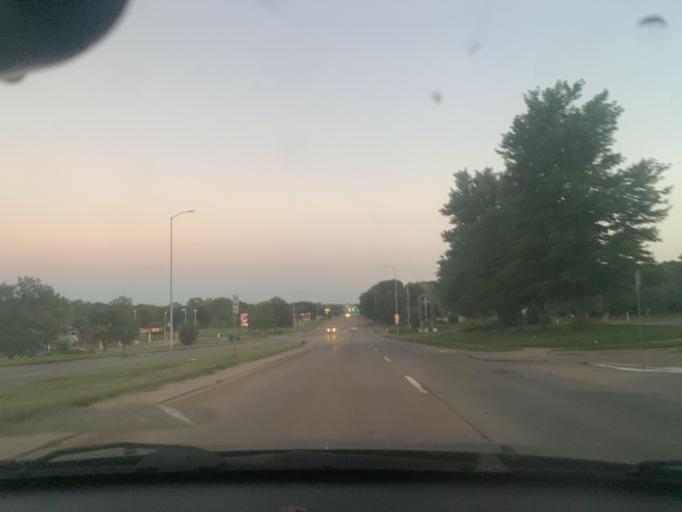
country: US
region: Nebraska
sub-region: Douglas County
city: Ralston
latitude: 41.3026
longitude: -96.0527
